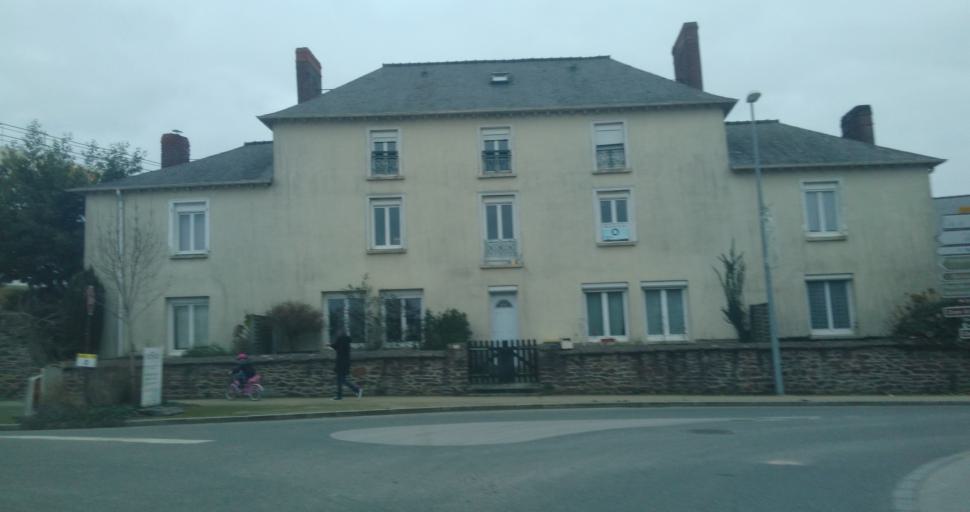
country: FR
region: Brittany
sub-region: Departement d'Ille-et-Vilaine
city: Romille
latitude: 48.2171
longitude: -1.8897
